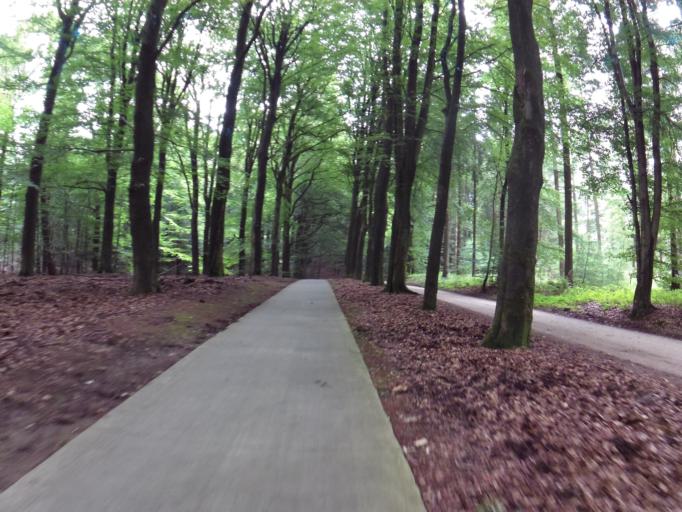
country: NL
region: Gelderland
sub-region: Gemeente Rheden
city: De Steeg
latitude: 52.0335
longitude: 6.0571
